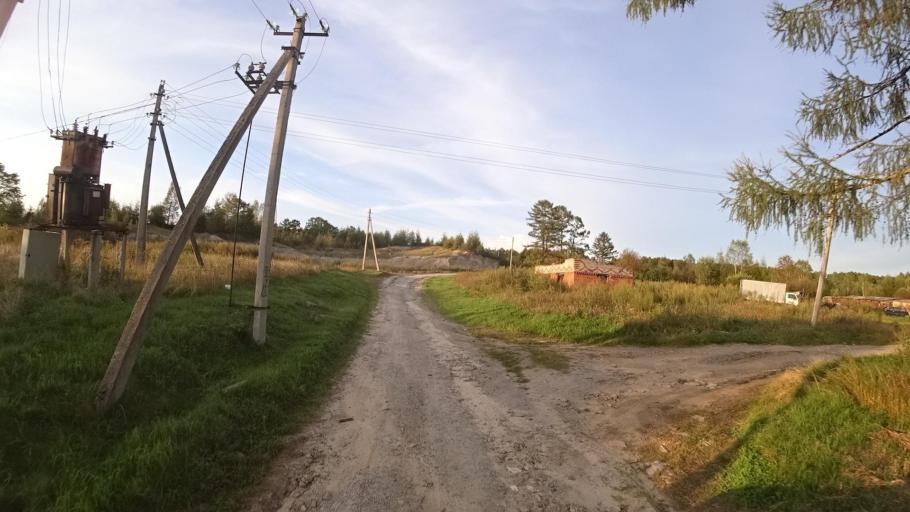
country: RU
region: Jewish Autonomous Oblast
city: Kul'dur
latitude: 49.2085
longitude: 131.6465
